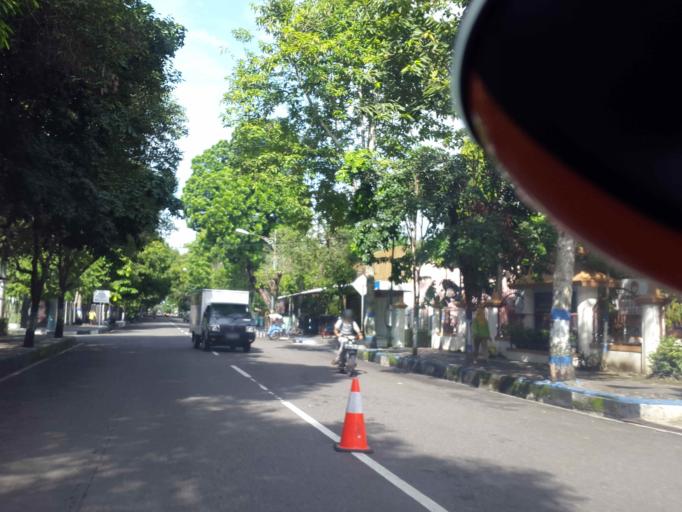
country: ID
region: Central Java
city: Wonosobo
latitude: -7.3953
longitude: 109.6986
